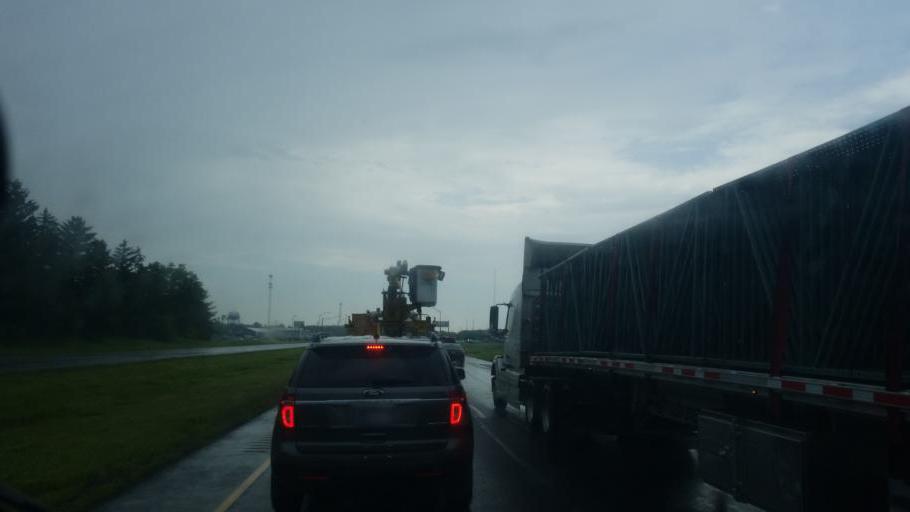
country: US
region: Indiana
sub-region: Whitley County
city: Columbia City
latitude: 41.1689
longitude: -85.4810
